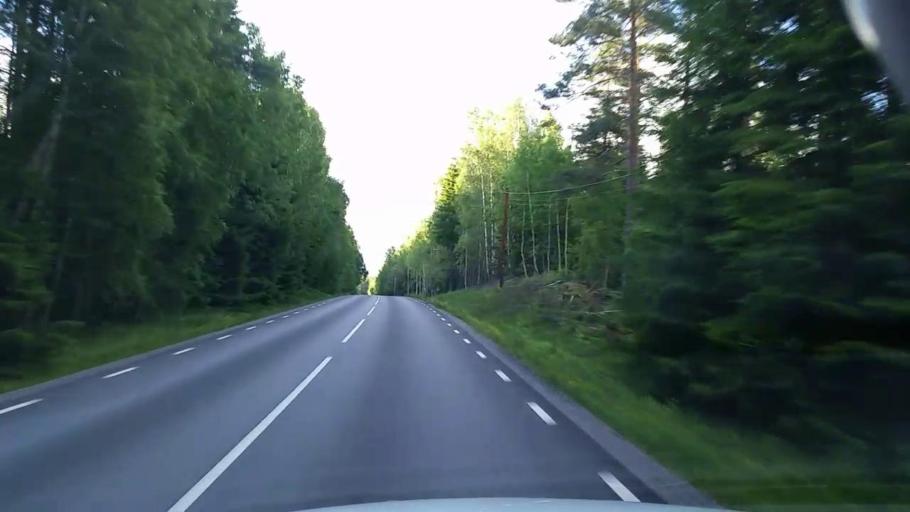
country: SE
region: Vaestmanland
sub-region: Kopings Kommun
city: Kolsva
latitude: 59.6473
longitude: 15.8326
